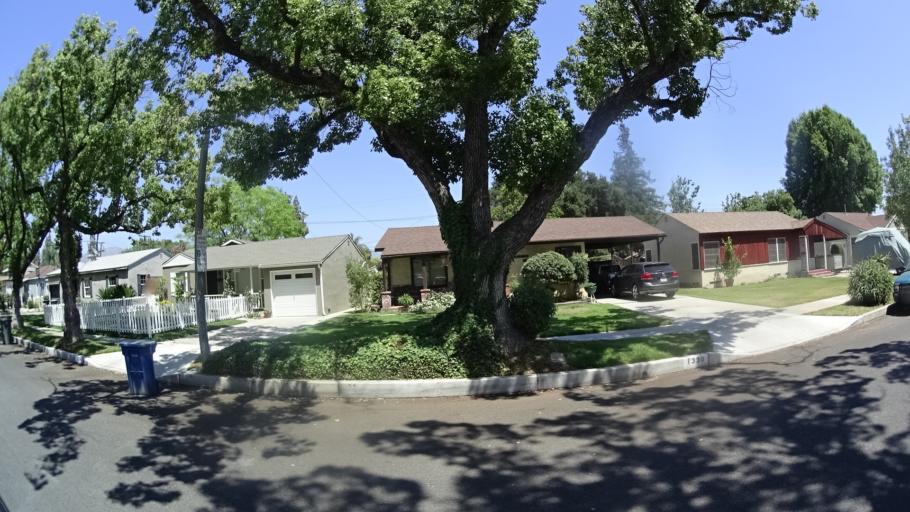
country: US
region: California
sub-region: Los Angeles County
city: Burbank
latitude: 34.1782
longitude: -118.3439
